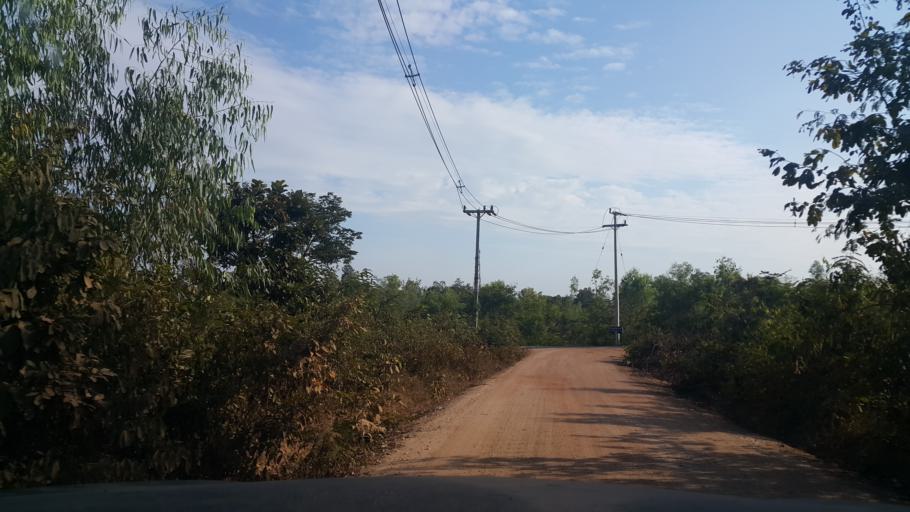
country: TH
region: Lampang
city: Hang Chat
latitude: 18.3004
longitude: 99.3527
